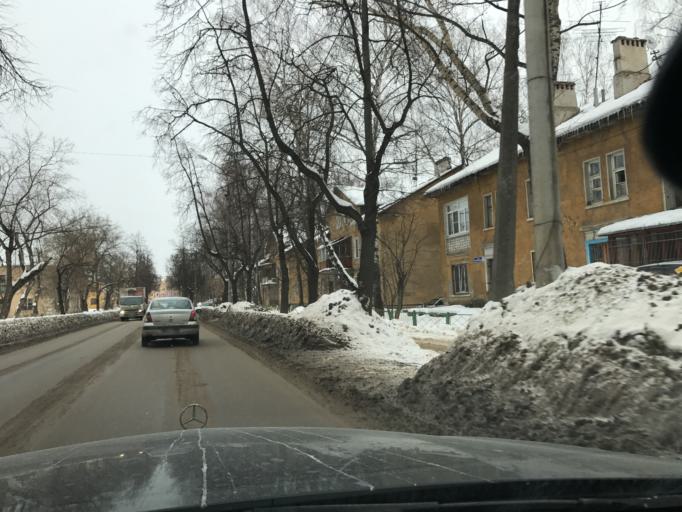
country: RU
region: Nizjnij Novgorod
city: Gorbatovka
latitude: 56.2458
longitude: 43.8287
